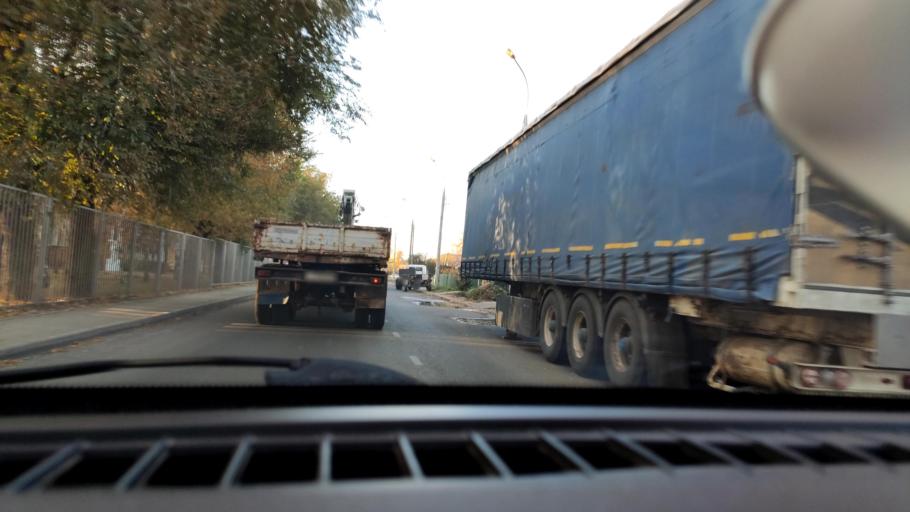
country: RU
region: Samara
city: Smyshlyayevka
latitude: 53.2307
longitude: 50.3086
